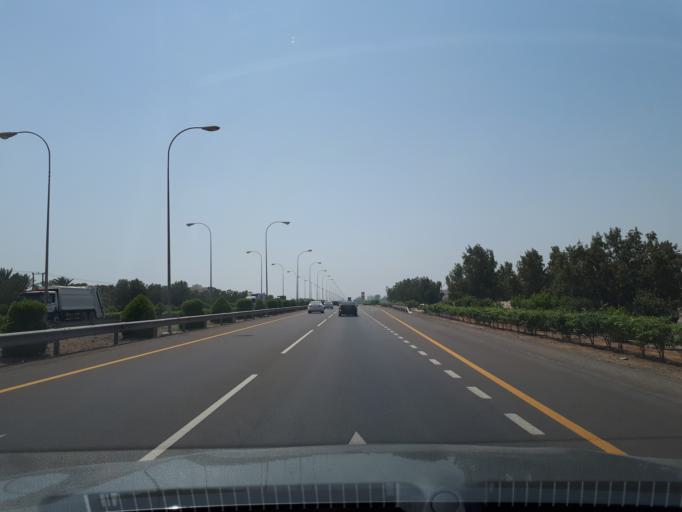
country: OM
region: Al Batinah
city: Al Sohar
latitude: 24.4015
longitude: 56.6622
